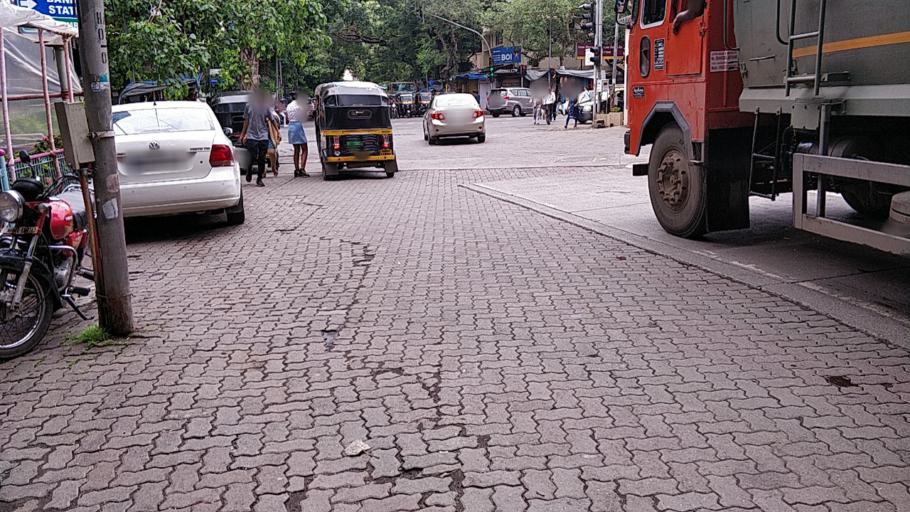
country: IN
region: Maharashtra
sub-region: Mumbai Suburban
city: Mumbai
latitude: 19.0679
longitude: 72.8332
